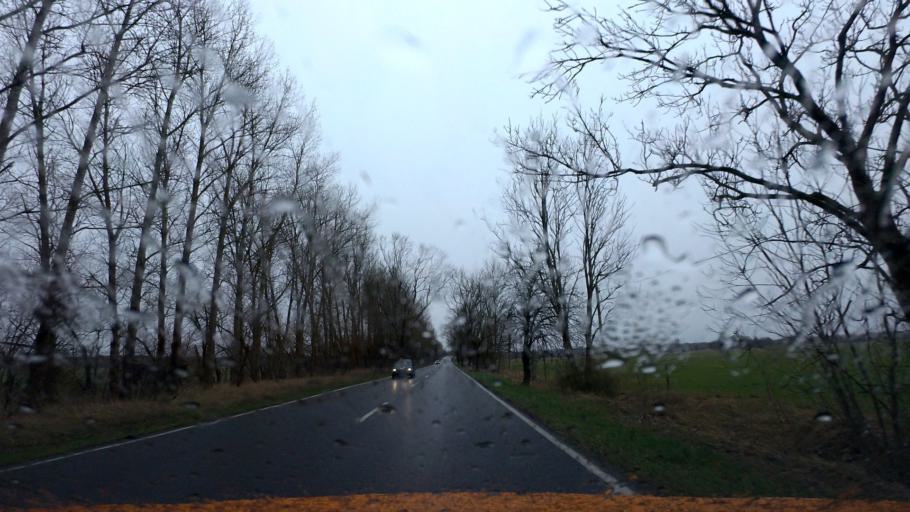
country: DE
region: Brandenburg
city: Velten
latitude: 52.6474
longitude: 13.1456
